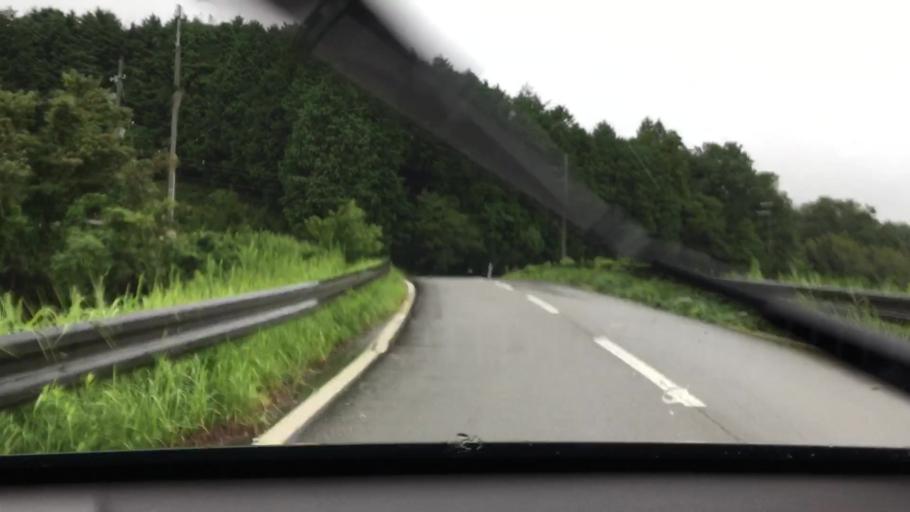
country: JP
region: Hyogo
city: Toyooka
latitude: 35.3095
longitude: 134.8736
